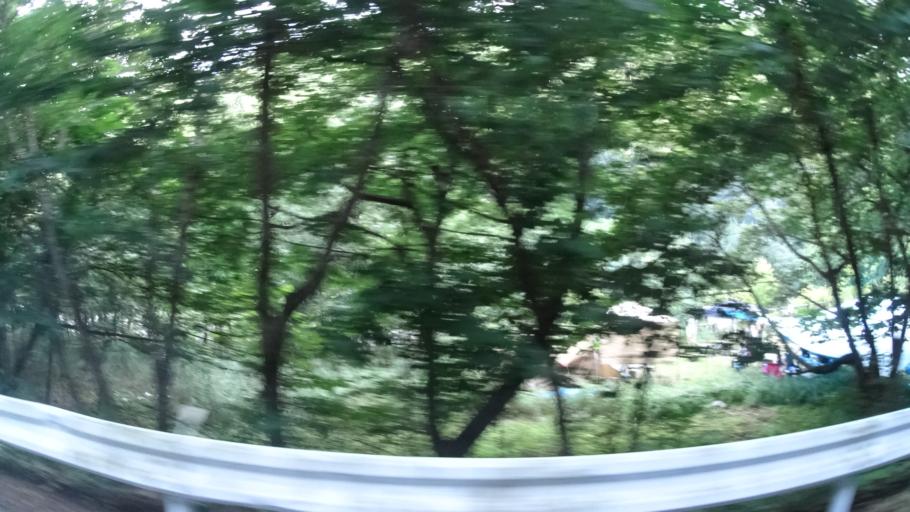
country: JP
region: Tochigi
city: Nikko
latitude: 36.6919
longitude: 139.4998
